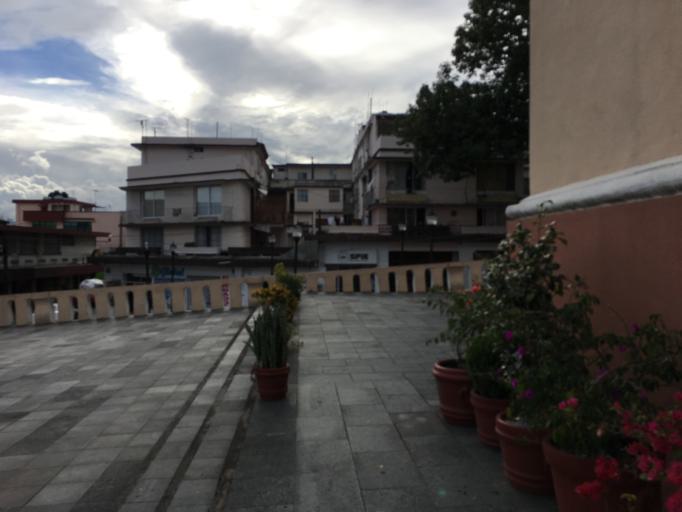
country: MX
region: Veracruz
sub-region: Xalapa
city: Xalapa de Enriquez
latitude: 19.5294
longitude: -96.9167
